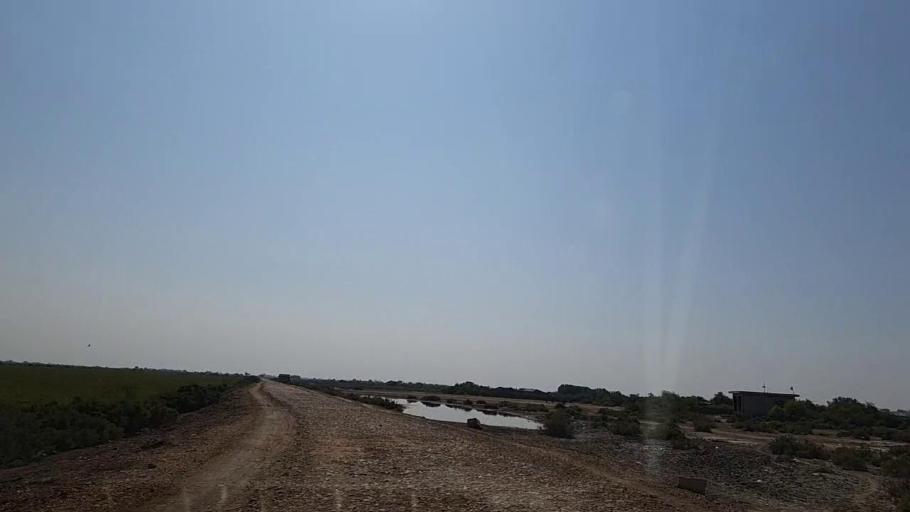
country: PK
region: Sindh
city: Chuhar Jamali
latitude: 24.4739
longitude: 68.0911
